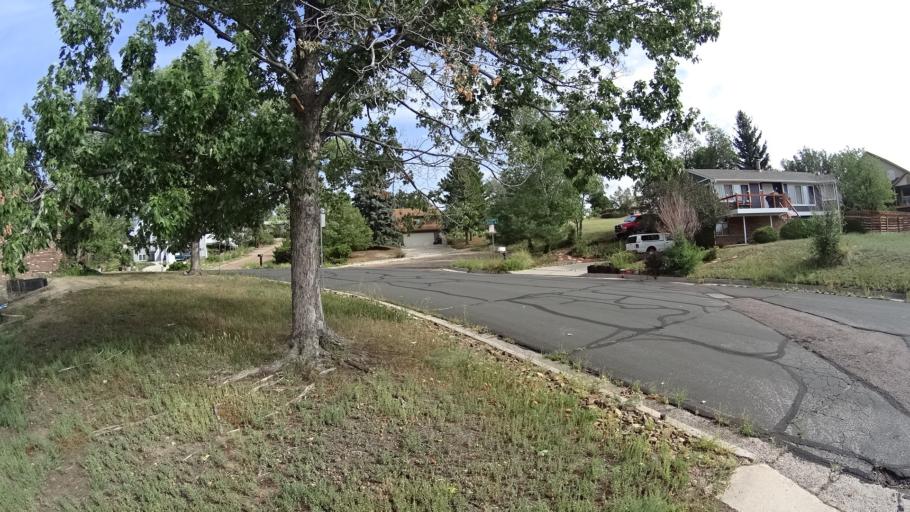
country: US
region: Colorado
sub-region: El Paso County
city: Colorado Springs
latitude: 38.8863
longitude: -104.7952
